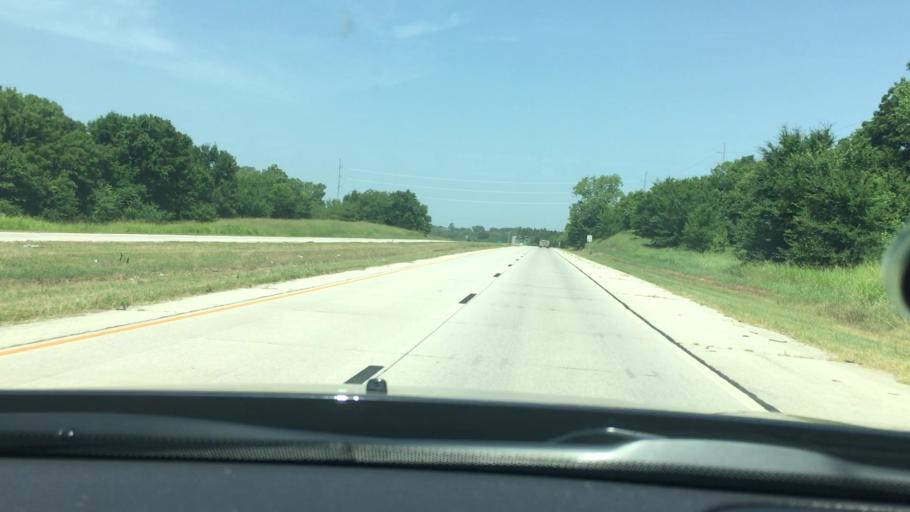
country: US
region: Oklahoma
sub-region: Pontotoc County
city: Ada
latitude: 34.7500
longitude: -96.6574
